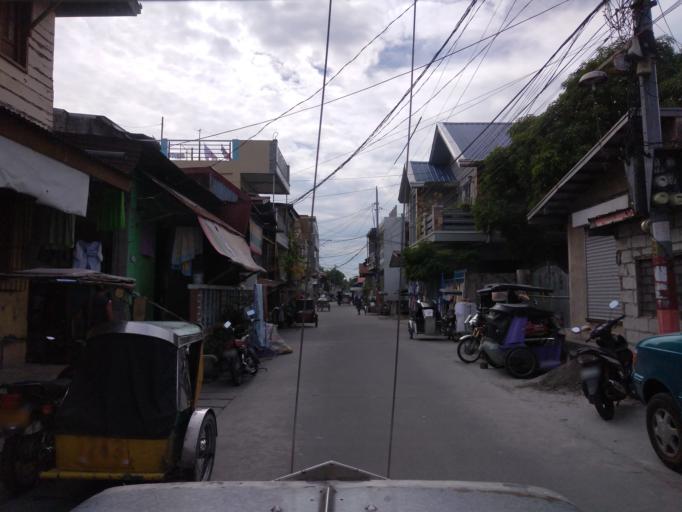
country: PH
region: Central Luzon
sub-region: Province of Pampanga
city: Sexmoan
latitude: 14.9347
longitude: 120.6234
